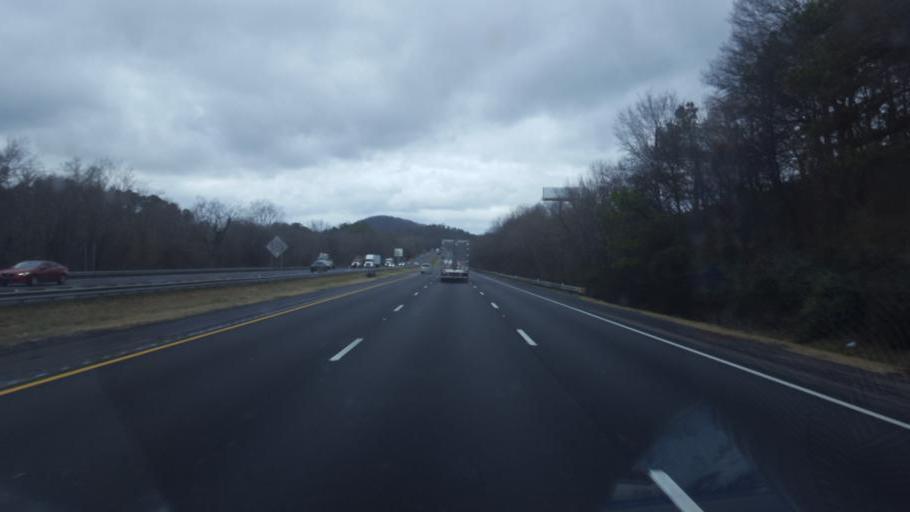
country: US
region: Georgia
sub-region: Whitfield County
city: Dalton
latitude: 34.7998
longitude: -85.0060
